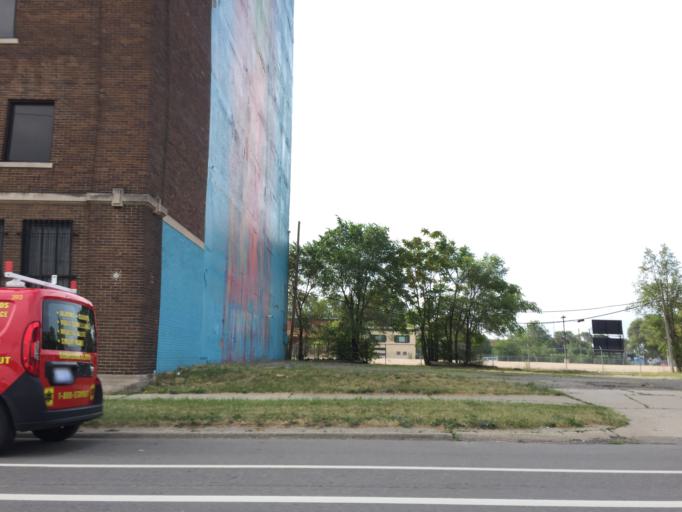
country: US
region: Michigan
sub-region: Wayne County
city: Hamtramck
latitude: 42.3722
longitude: -83.0679
